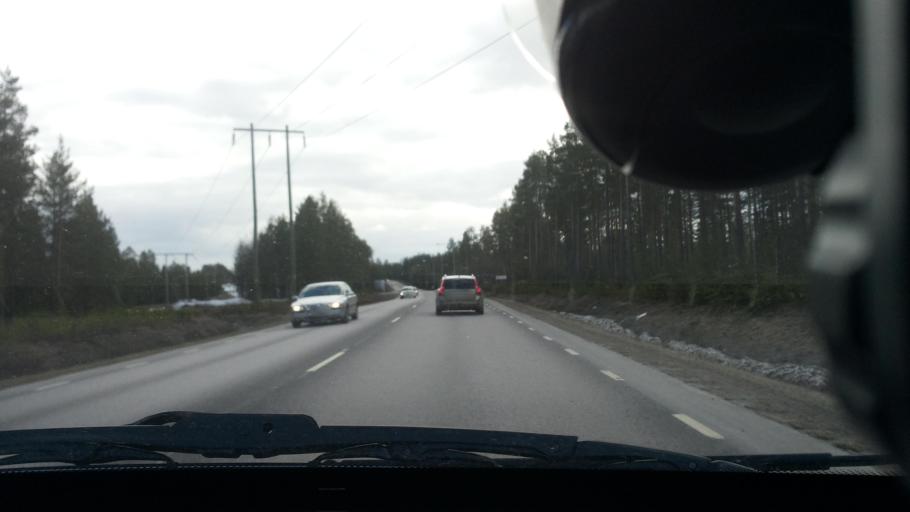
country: SE
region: Norrbotten
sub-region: Lulea Kommun
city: Gammelstad
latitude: 65.6105
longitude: 22.0412
